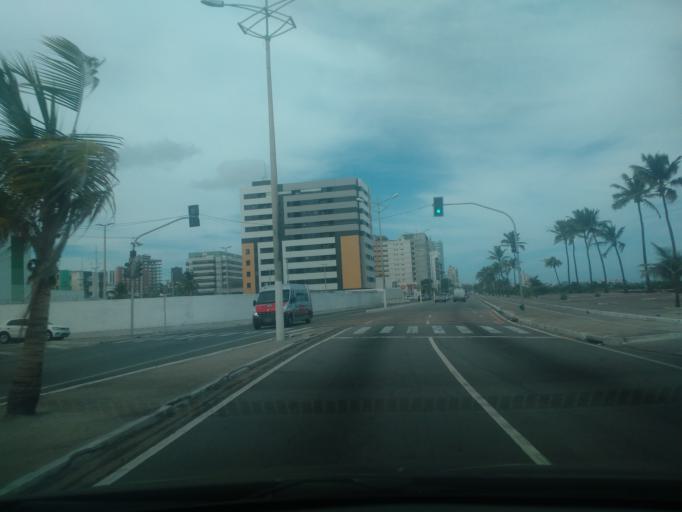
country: BR
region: Alagoas
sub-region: Maceio
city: Maceio
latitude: -9.6707
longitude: -35.7421
